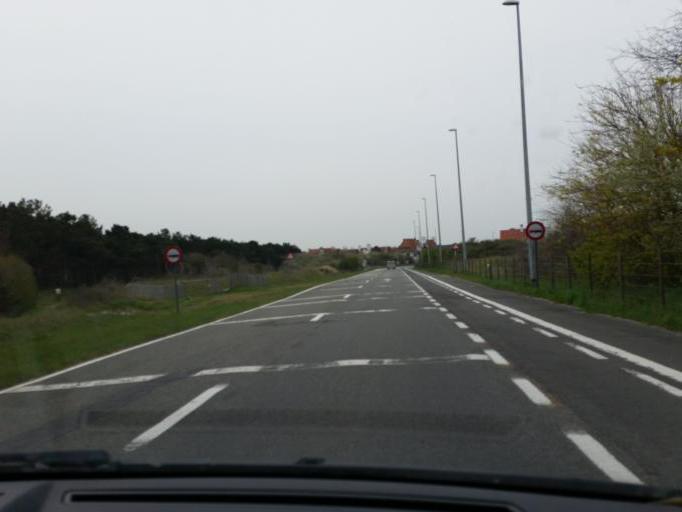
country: BE
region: Flanders
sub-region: Provincie West-Vlaanderen
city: De Haan
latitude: 51.2819
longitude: 3.0421
